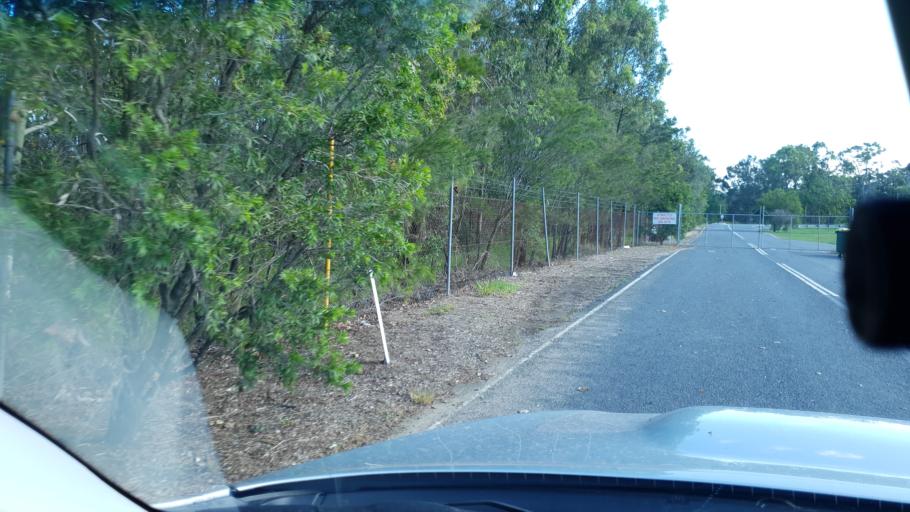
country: AU
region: Queensland
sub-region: Logan
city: Woodridge
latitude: -27.6730
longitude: 153.0703
